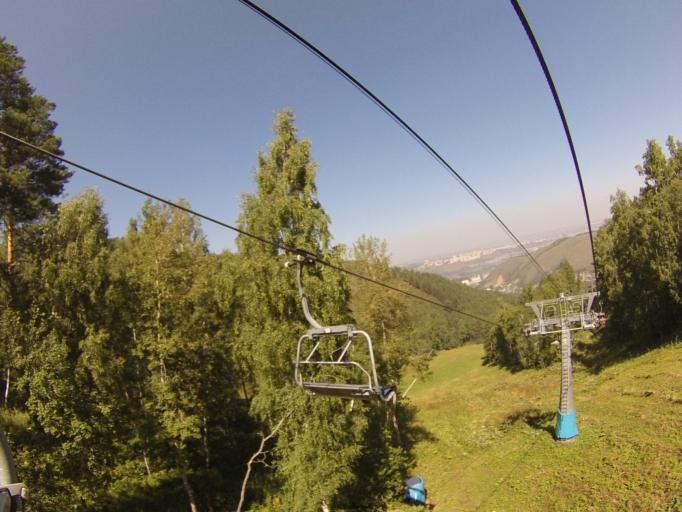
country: RU
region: Krasnoyarskiy
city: Krasnoyarsk
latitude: 55.9513
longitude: 92.7883
